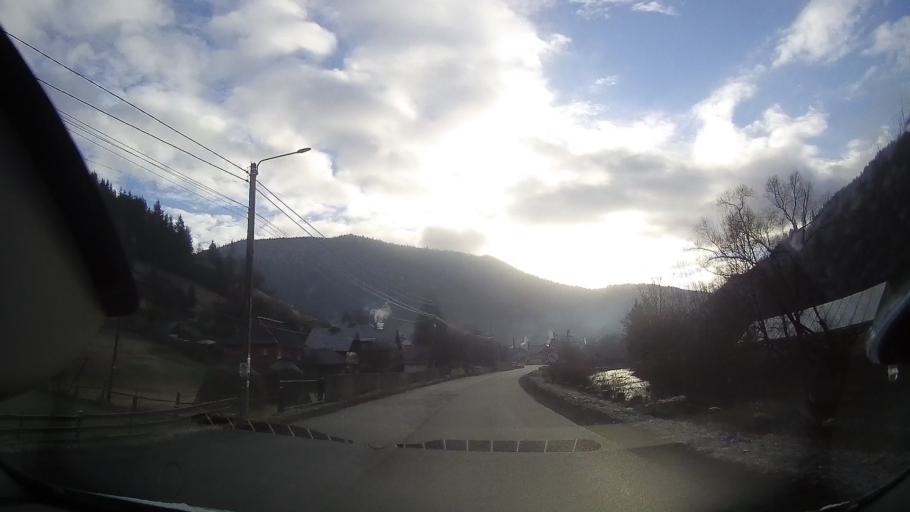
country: RO
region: Alba
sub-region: Comuna Albac
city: Albac
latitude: 46.4511
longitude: 22.9601
